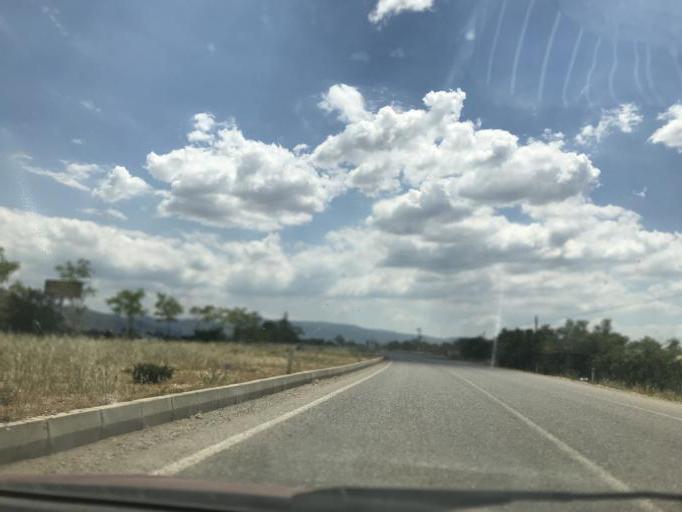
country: TR
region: Denizli
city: Tavas
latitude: 37.5529
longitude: 29.0529
